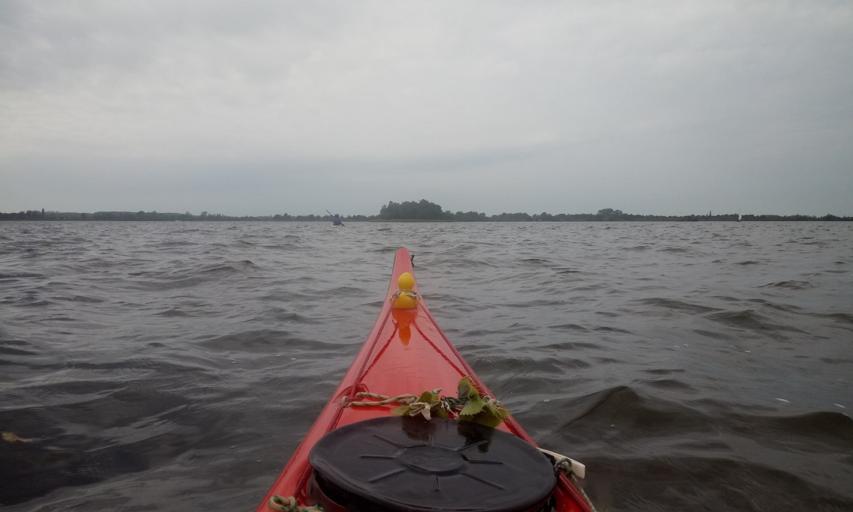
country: NL
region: North Holland
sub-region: Gemeente Wijdemeren
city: Oud-Loosdrecht
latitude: 52.1838
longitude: 5.0600
